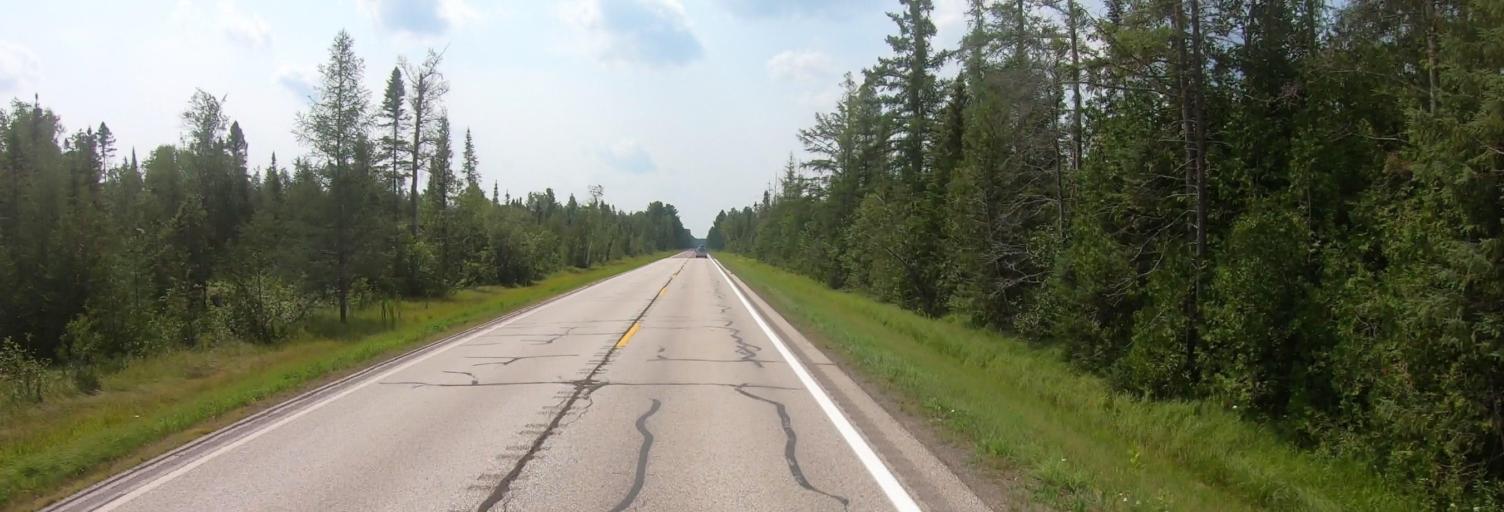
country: US
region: Michigan
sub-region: Luce County
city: Newberry
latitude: 46.4871
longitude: -85.4268
